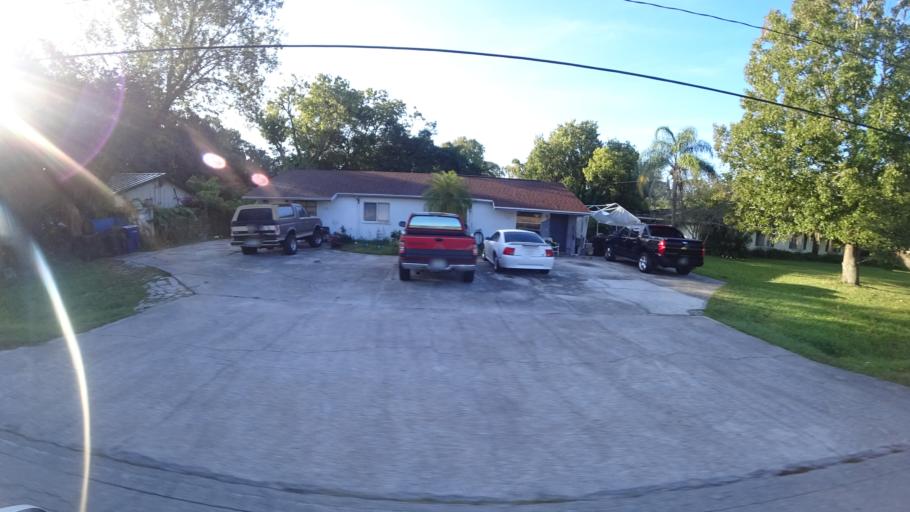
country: US
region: Florida
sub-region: Manatee County
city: Samoset
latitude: 27.4509
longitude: -82.5233
